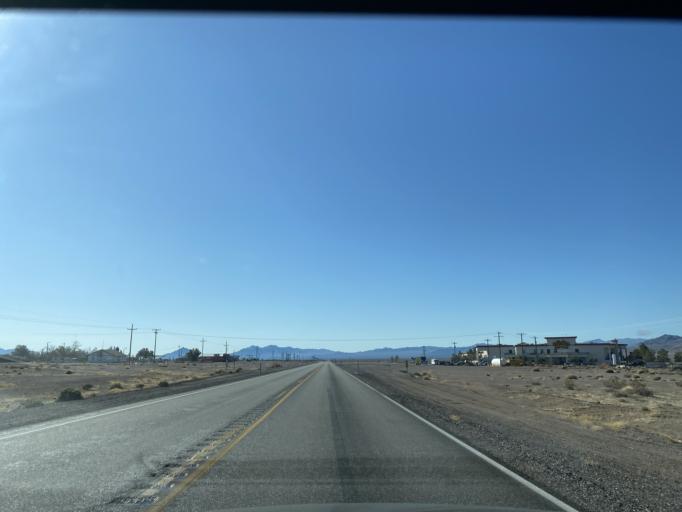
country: US
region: Nevada
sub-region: Nye County
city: Pahrump
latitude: 36.4156
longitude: -116.4223
